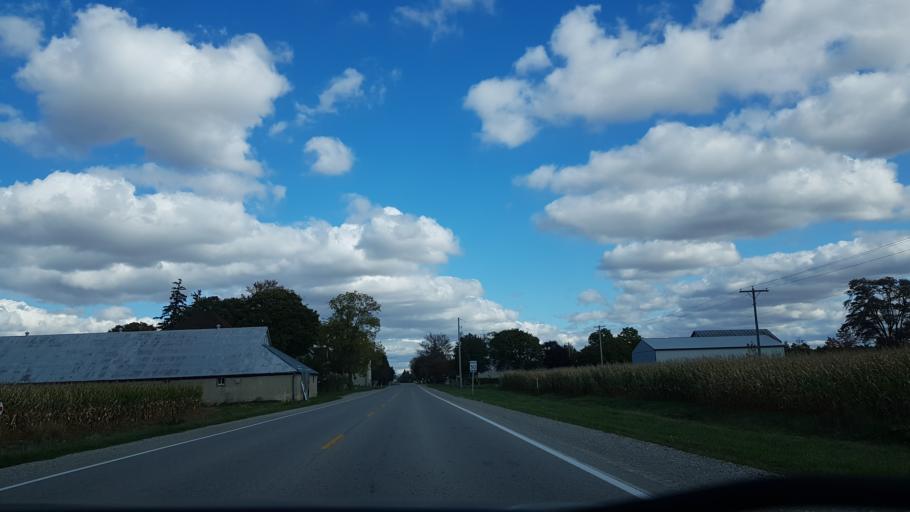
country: CA
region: Ontario
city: South Huron
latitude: 43.2426
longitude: -81.7195
